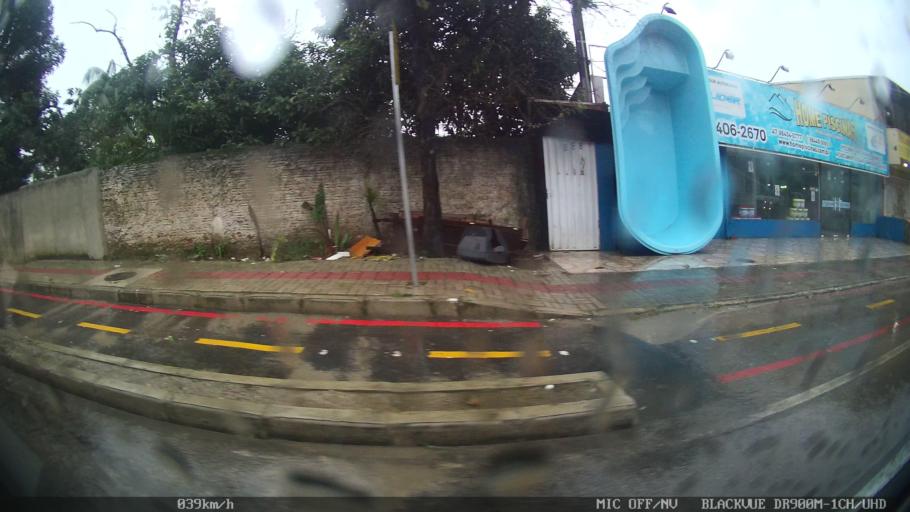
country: BR
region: Santa Catarina
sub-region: Balneario Camboriu
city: Balneario Camboriu
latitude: -27.0059
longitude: -48.6472
